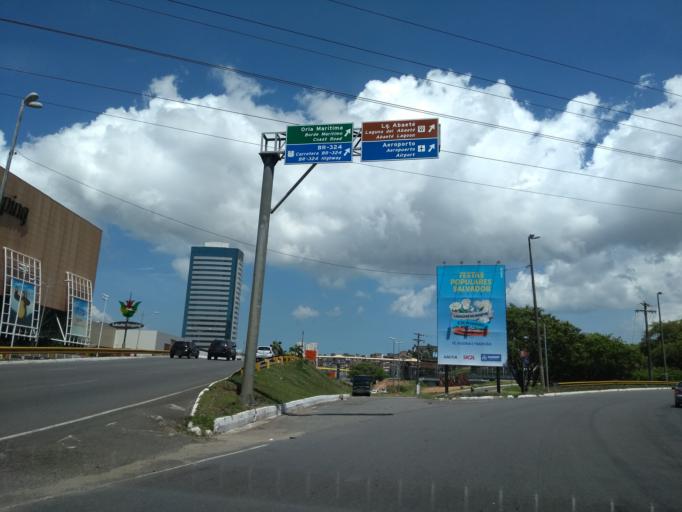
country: BR
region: Bahia
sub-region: Salvador
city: Salvador
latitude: -12.9776
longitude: -38.4536
